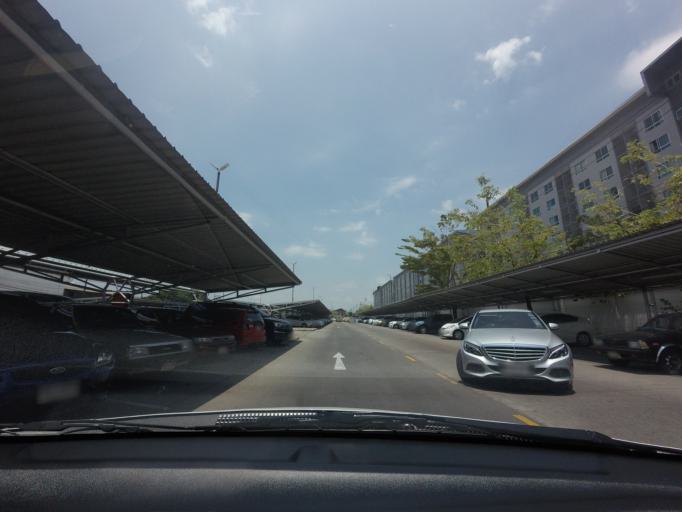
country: TH
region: Bangkok
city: Khan Na Yao
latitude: 13.8240
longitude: 100.6572
